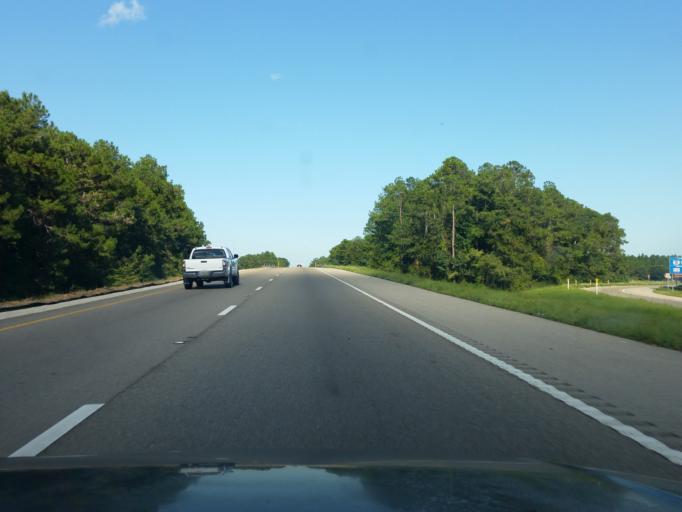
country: US
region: Mississippi
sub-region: Hancock County
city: Pearlington
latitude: 30.3146
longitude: -89.6006
